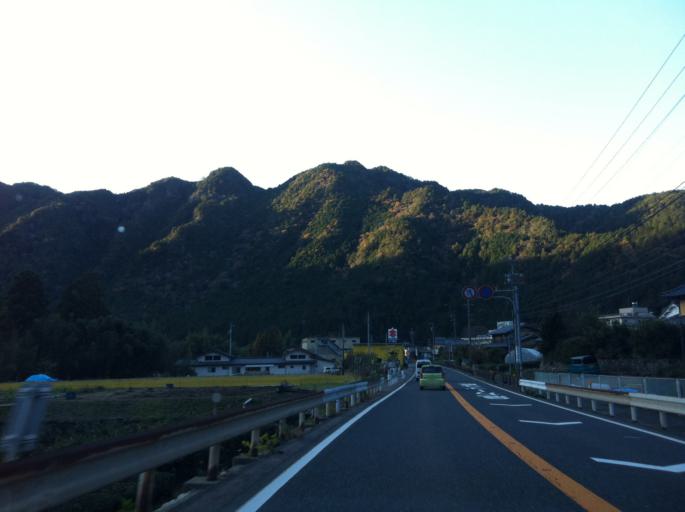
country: JP
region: Gifu
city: Mitake
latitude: 35.6004
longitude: 137.1674
